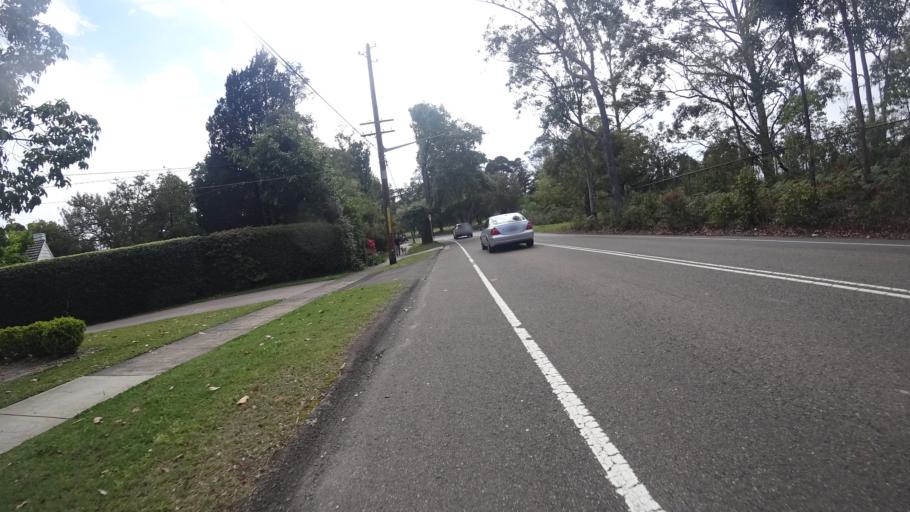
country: AU
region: New South Wales
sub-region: City of Sydney
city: North Turramurra
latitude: -33.7024
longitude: 151.1472
